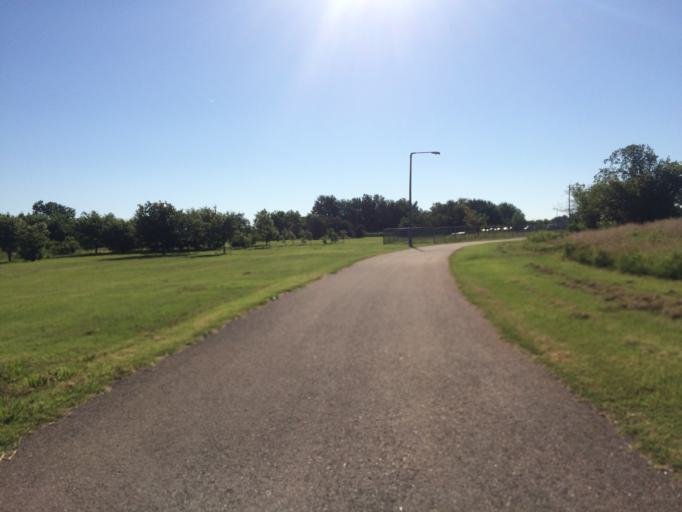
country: US
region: Oklahoma
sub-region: Cleveland County
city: Norman
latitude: 35.2383
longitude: -97.4290
